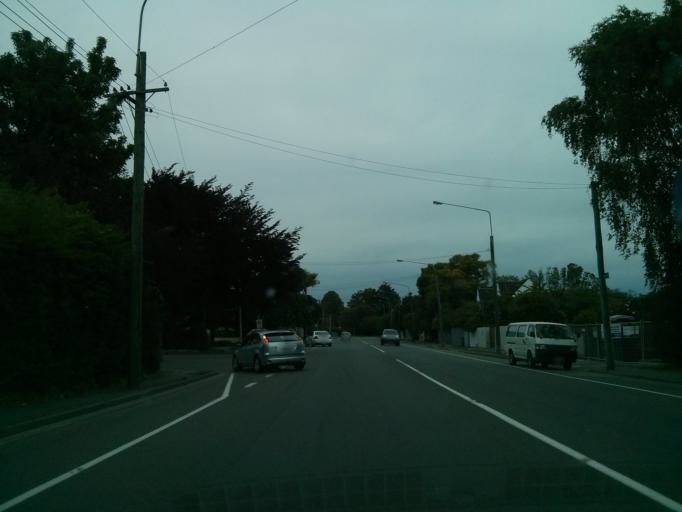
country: NZ
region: Canterbury
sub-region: Christchurch City
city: Christchurch
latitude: -43.5159
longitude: 172.6032
